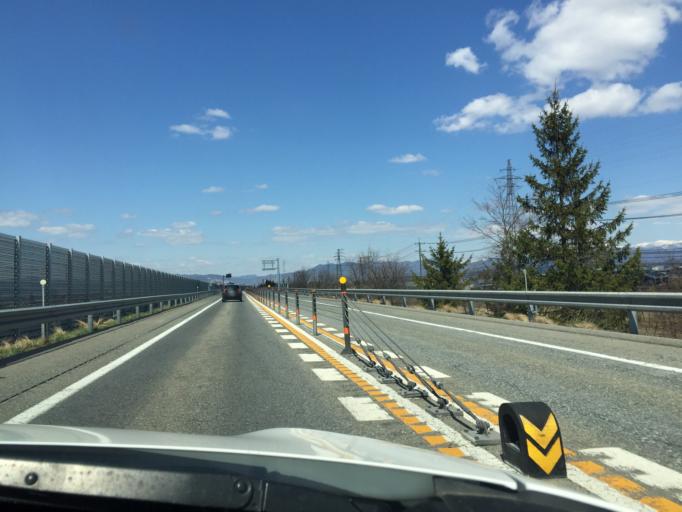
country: JP
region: Yamagata
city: Yonezawa
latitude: 37.9615
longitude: 140.1197
